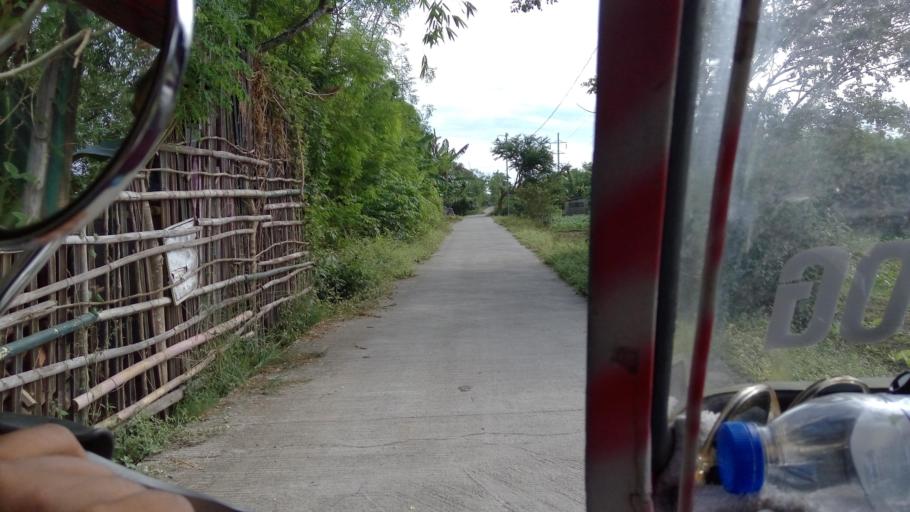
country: PH
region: Ilocos
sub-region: Province of La Union
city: San Eugenio
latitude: 16.3678
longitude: 120.3524
